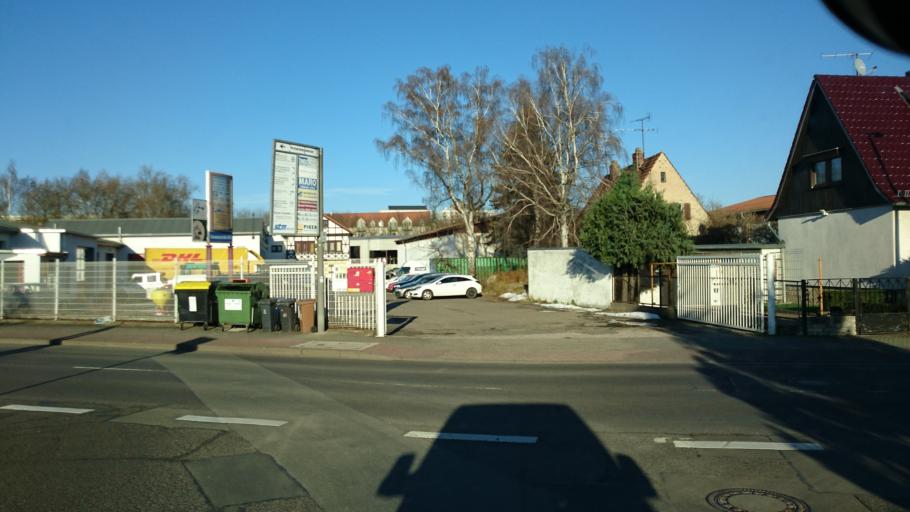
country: DE
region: Thuringia
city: Weimar
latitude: 50.9833
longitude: 11.3049
